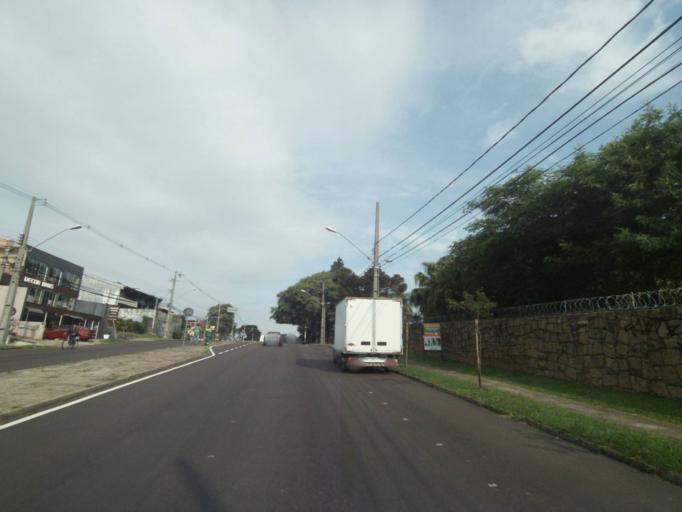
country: BR
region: Parana
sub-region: Curitiba
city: Curitiba
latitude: -25.4137
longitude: -49.3124
